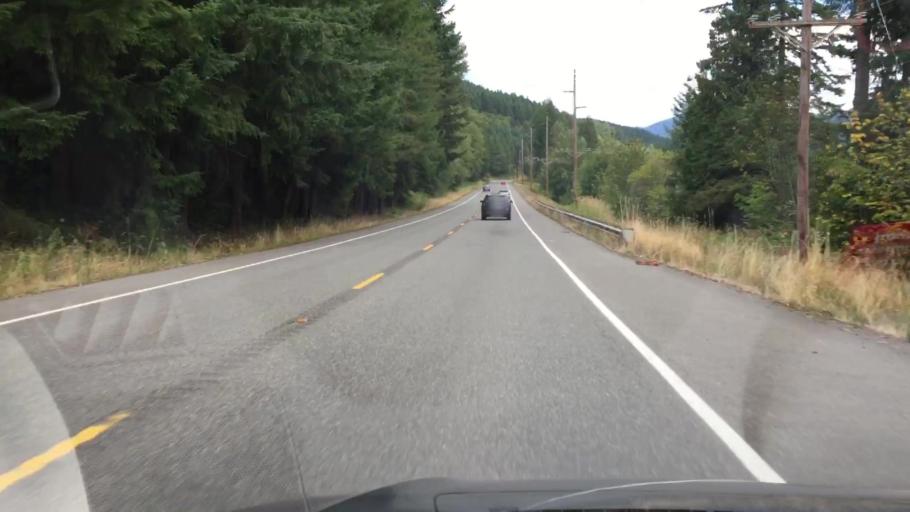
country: US
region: Washington
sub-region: Pierce County
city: Eatonville
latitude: 46.7820
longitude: -122.2392
